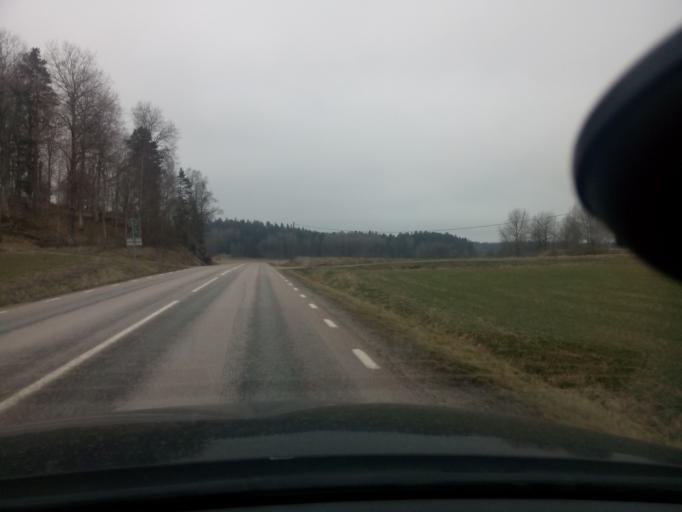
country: SE
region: Soedermanland
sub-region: Gnesta Kommun
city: Gnesta
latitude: 59.0403
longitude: 17.1613
